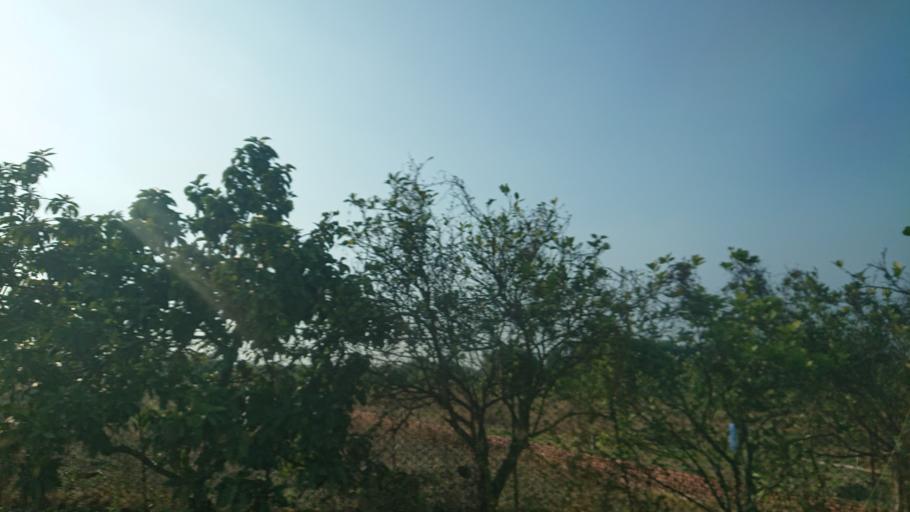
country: TW
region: Taiwan
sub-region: Tainan
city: Tainan
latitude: 23.1451
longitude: 120.2461
